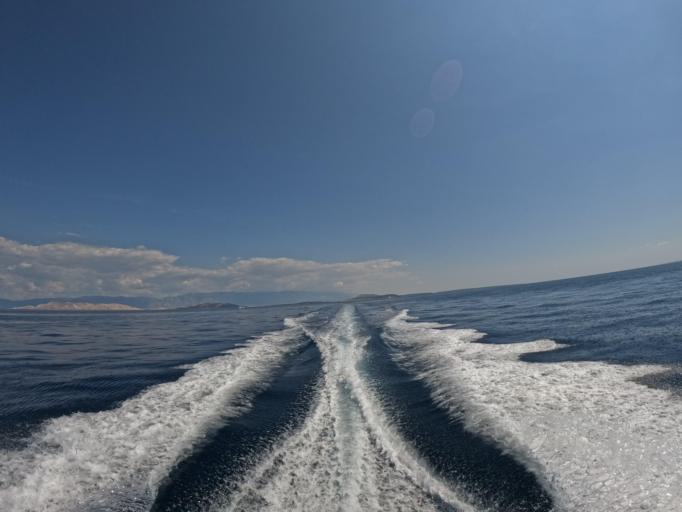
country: HR
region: Primorsko-Goranska
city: Punat
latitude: 44.8984
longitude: 14.6164
